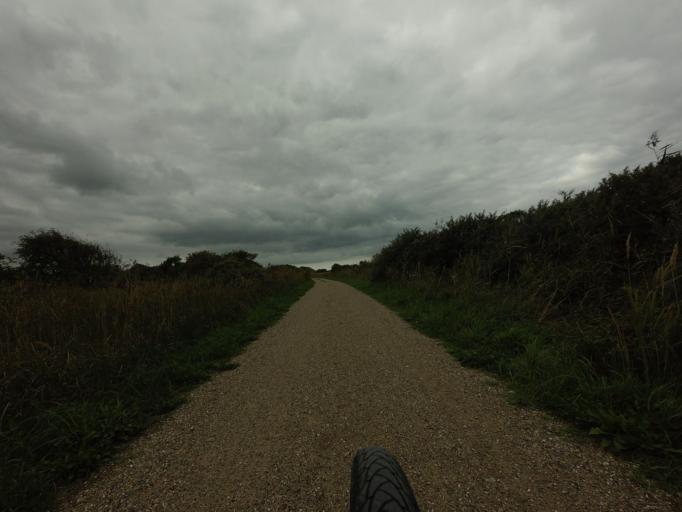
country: DK
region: North Denmark
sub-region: Hjorring Kommune
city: Sindal
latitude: 57.5888
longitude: 10.1406
